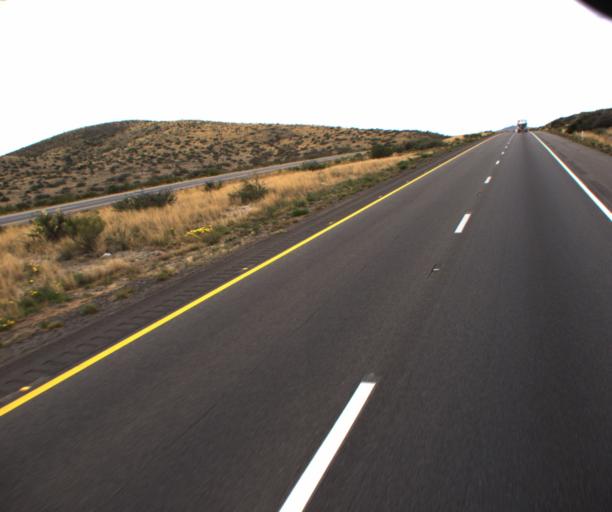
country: US
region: Arizona
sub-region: Cochise County
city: Willcox
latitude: 32.1166
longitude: -110.0198
